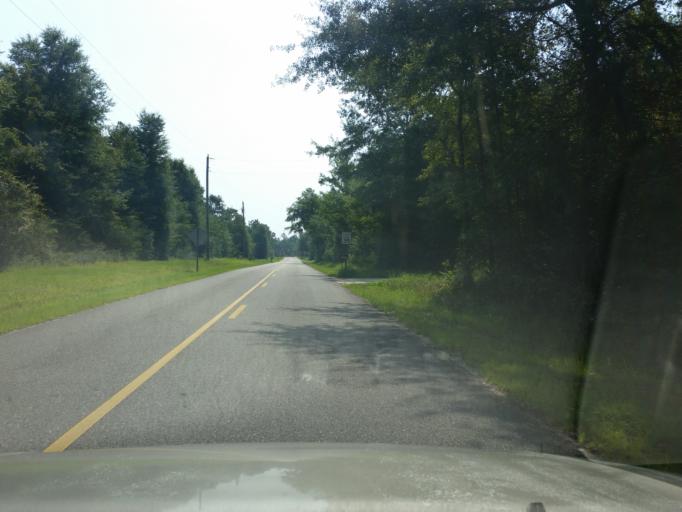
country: US
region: Florida
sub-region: Escambia County
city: Bellview
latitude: 30.5112
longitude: -87.4628
